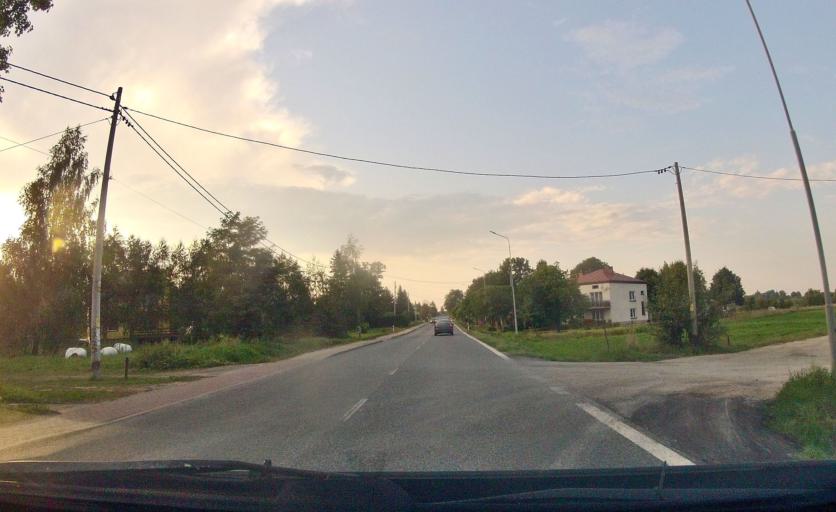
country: PL
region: Subcarpathian Voivodeship
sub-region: Powiat jasielski
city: Nowy Zmigrod
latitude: 49.5978
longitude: 21.5320
